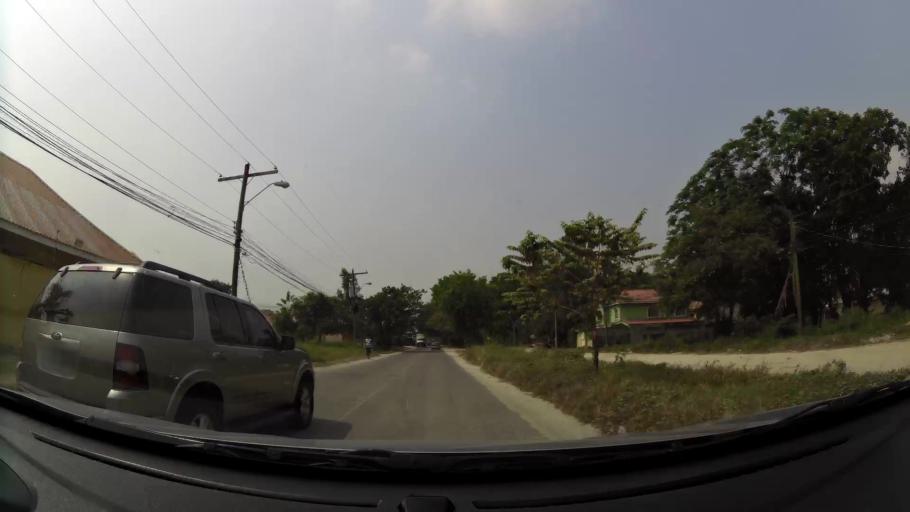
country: HN
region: Cortes
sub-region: San Pedro Sula
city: Pena Blanca
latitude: 15.5453
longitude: -88.0281
